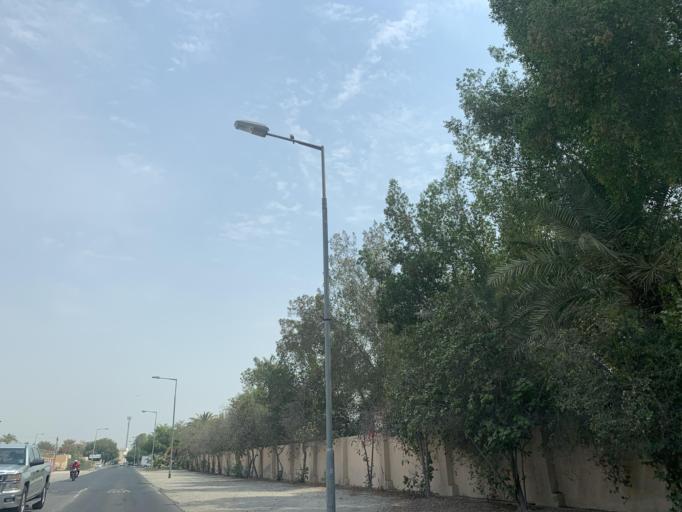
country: BH
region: Manama
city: Jidd Hafs
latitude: 26.2173
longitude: 50.4870
